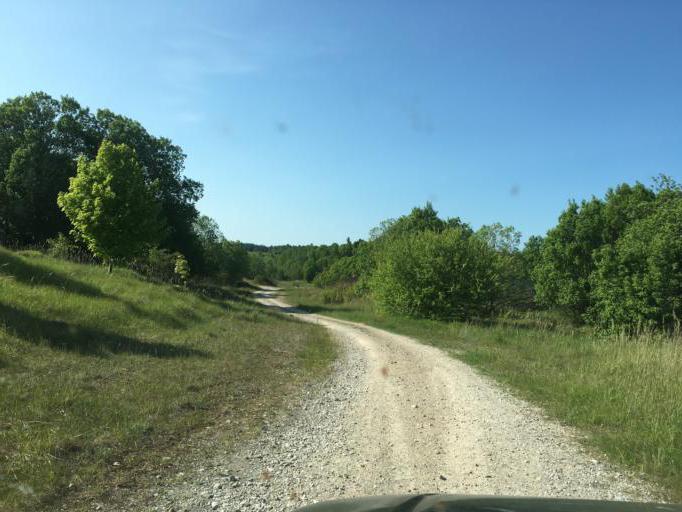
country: LV
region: Dundaga
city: Dundaga
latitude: 57.6102
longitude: 22.4421
